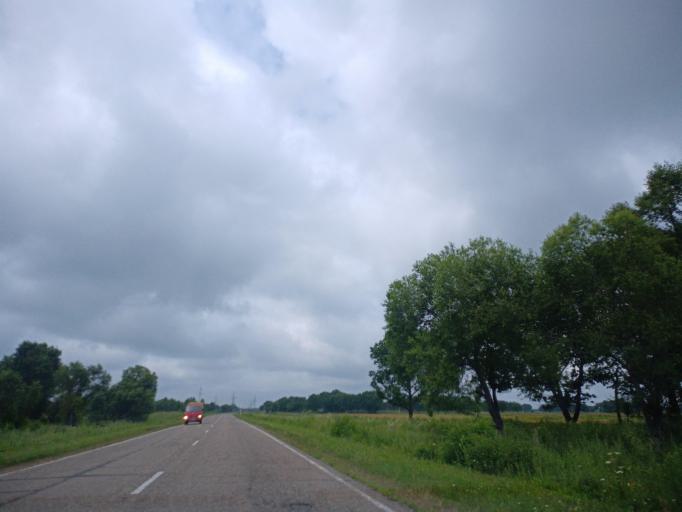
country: RU
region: Primorskiy
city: Dal'nerechensk
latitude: 45.9498
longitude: 133.9203
